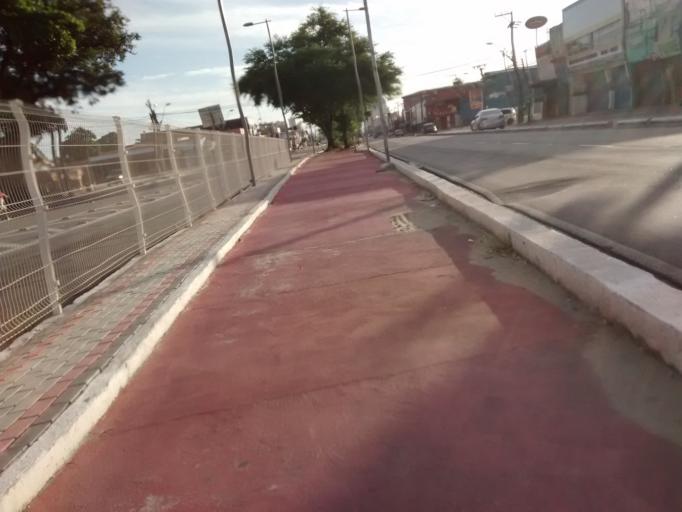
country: BR
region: Ceara
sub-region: Fortaleza
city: Fortaleza
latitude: -3.7314
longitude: -38.5440
